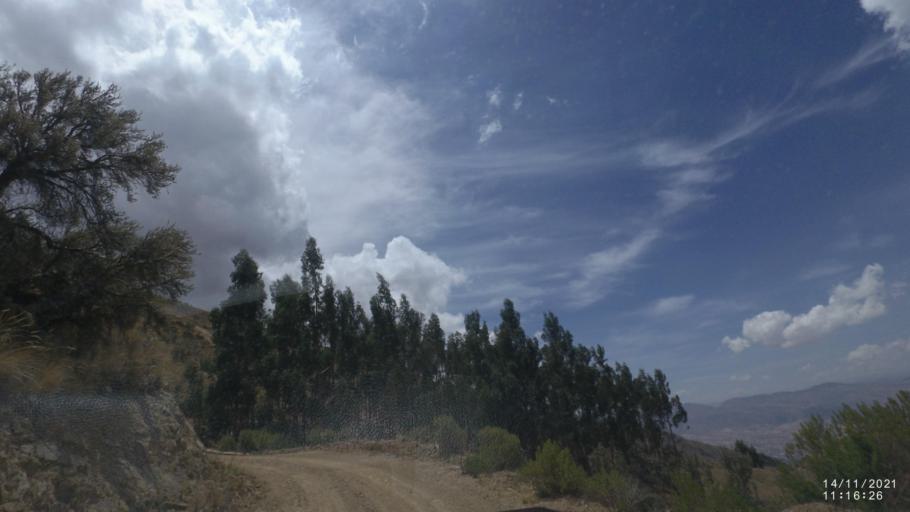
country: BO
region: Cochabamba
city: Cochabamba
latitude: -17.3287
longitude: -66.0477
